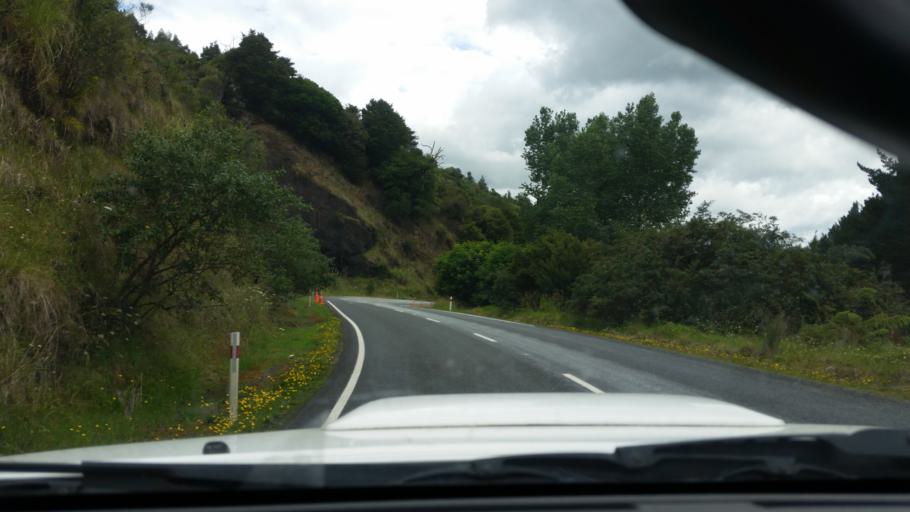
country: NZ
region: Northland
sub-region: Kaipara District
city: Dargaville
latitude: -35.7700
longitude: 173.9087
